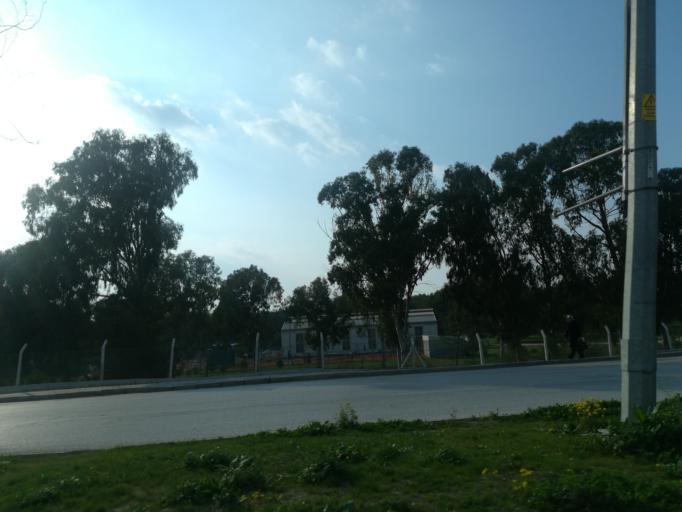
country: TR
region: Adana
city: Adana
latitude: 37.0286
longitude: 35.3450
